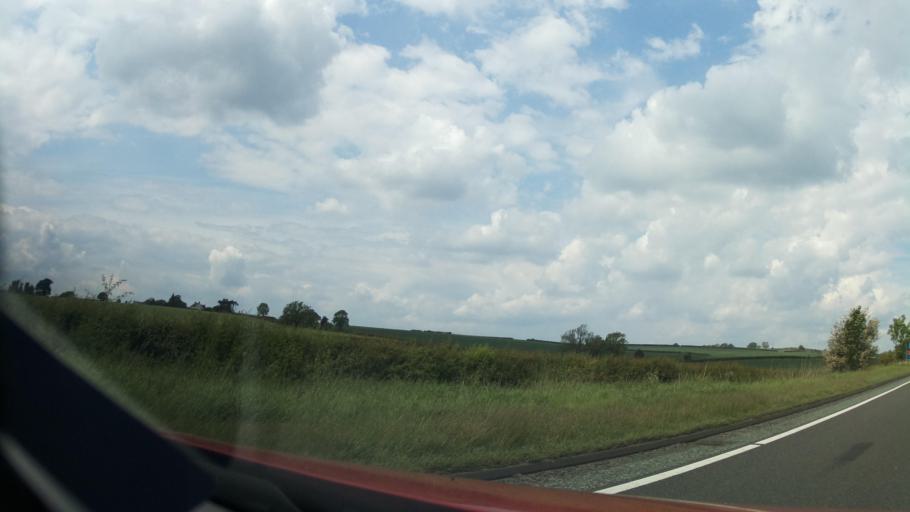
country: GB
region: England
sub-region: North Yorkshire
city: Thirsk
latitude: 54.3101
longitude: -1.3380
